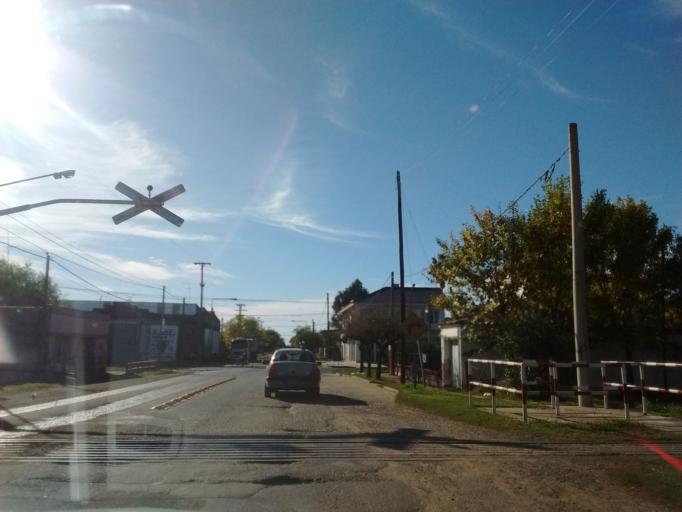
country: AR
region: Santa Fe
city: Coronda
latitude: -32.2311
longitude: -60.9809
